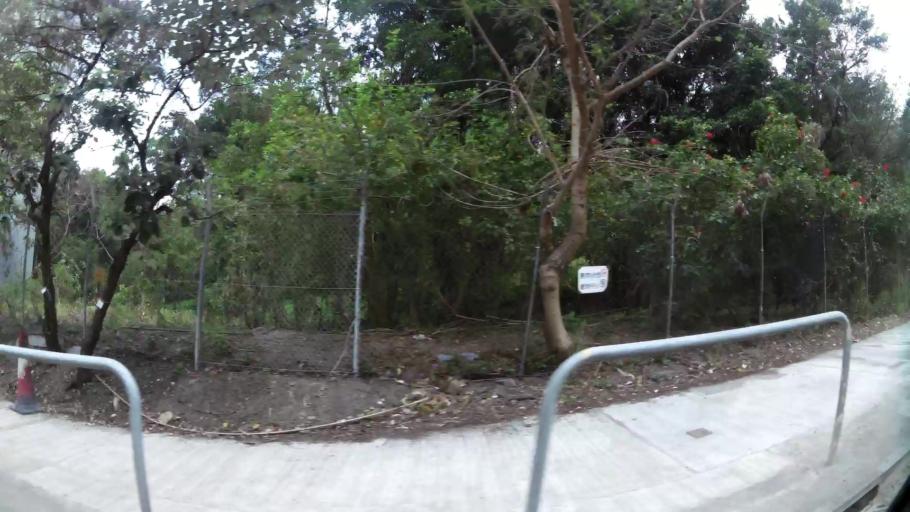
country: HK
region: Kowloon City
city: Kowloon
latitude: 22.3134
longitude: 114.2376
